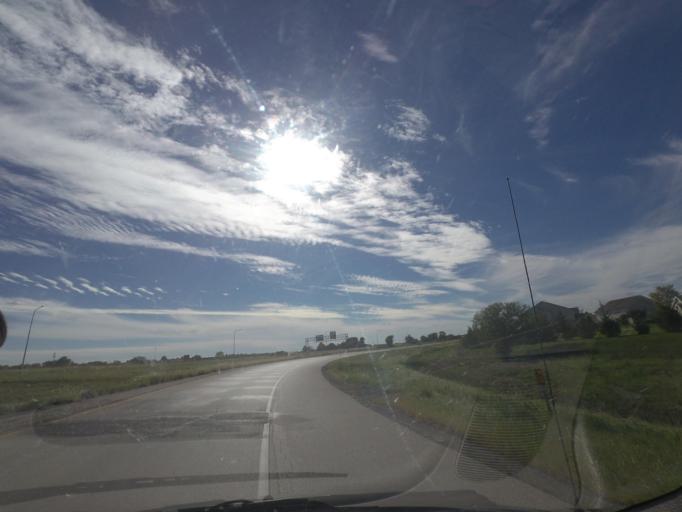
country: US
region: Illinois
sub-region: Champaign County
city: Champaign
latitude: 40.1207
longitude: -88.3079
